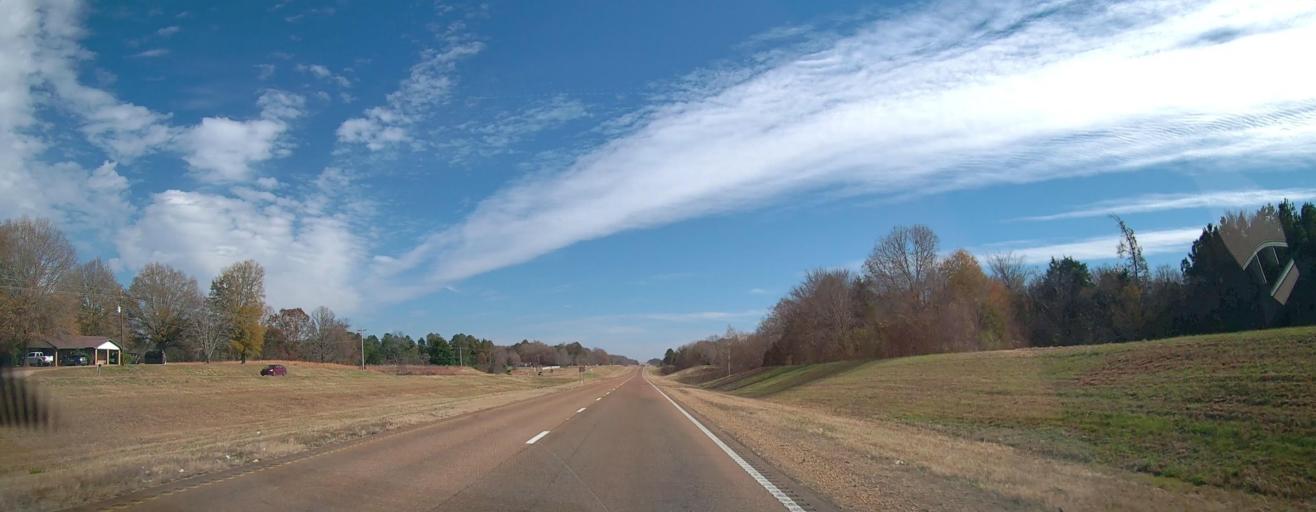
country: US
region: Mississippi
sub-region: Marshall County
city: Holly Springs
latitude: 34.9461
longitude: -89.3614
